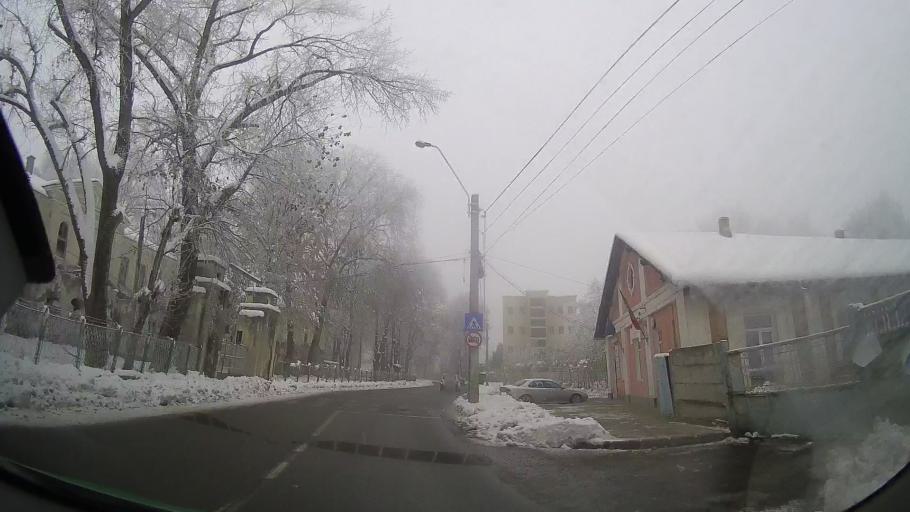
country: RO
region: Neamt
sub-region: Municipiul Roman
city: Roman
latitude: 46.9321
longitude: 26.9163
